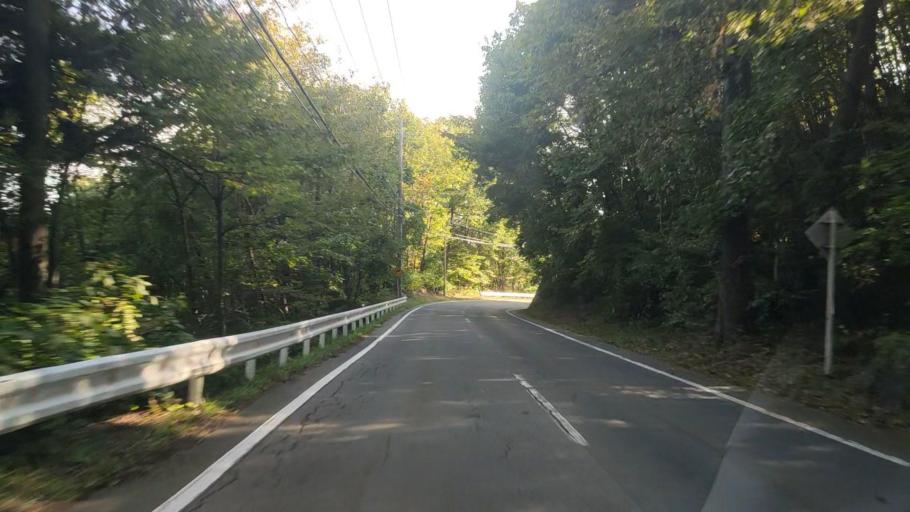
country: JP
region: Nagano
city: Suzaka
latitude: 36.5471
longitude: 138.5568
